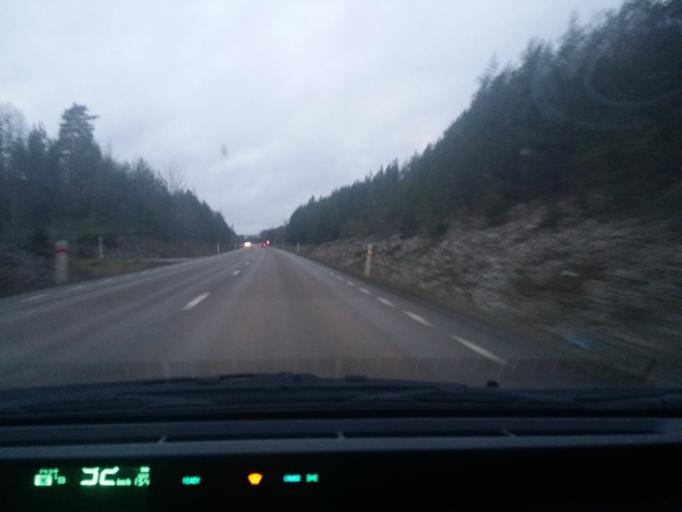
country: SE
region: Soedermanland
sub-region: Eskilstuna Kommun
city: Kvicksund
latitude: 59.4904
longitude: 16.3053
